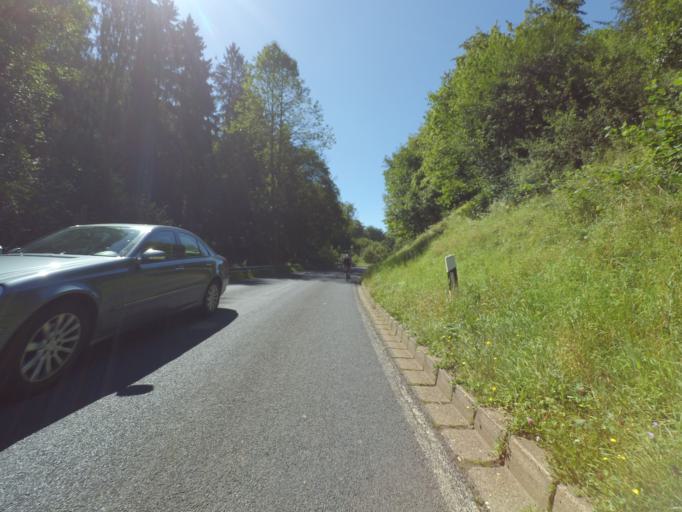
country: DE
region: Rheinland-Pfalz
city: Schutz
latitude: 50.1320
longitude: 6.7406
